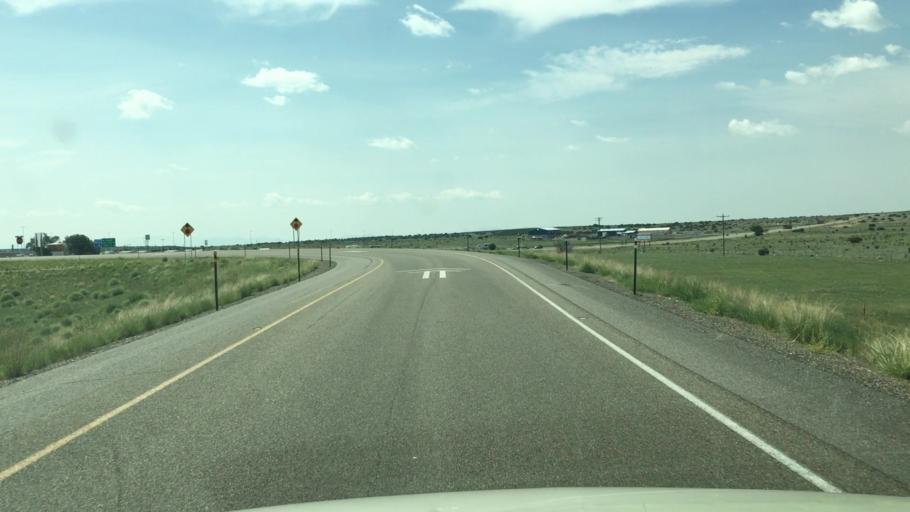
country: US
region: New Mexico
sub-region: Torrance County
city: Moriarty
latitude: 35.0093
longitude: -105.6628
